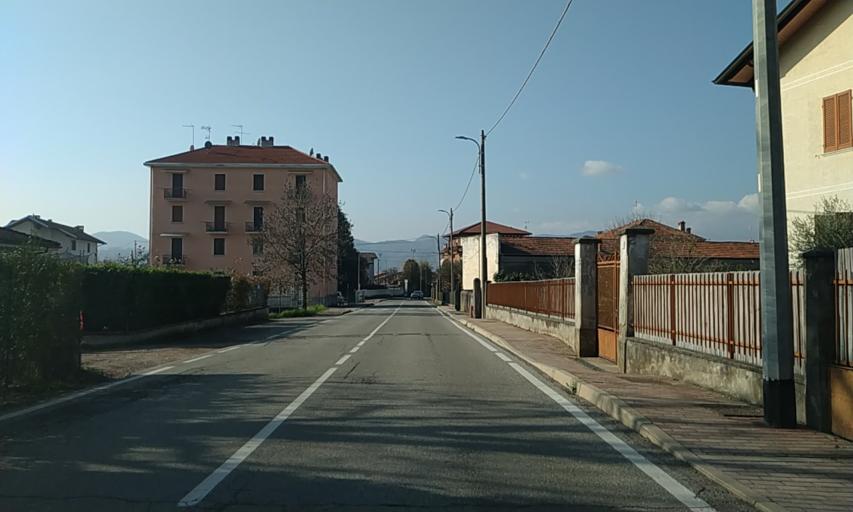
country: IT
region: Piedmont
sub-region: Provincia di Novara
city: Grignasco
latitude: 45.6815
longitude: 8.3486
